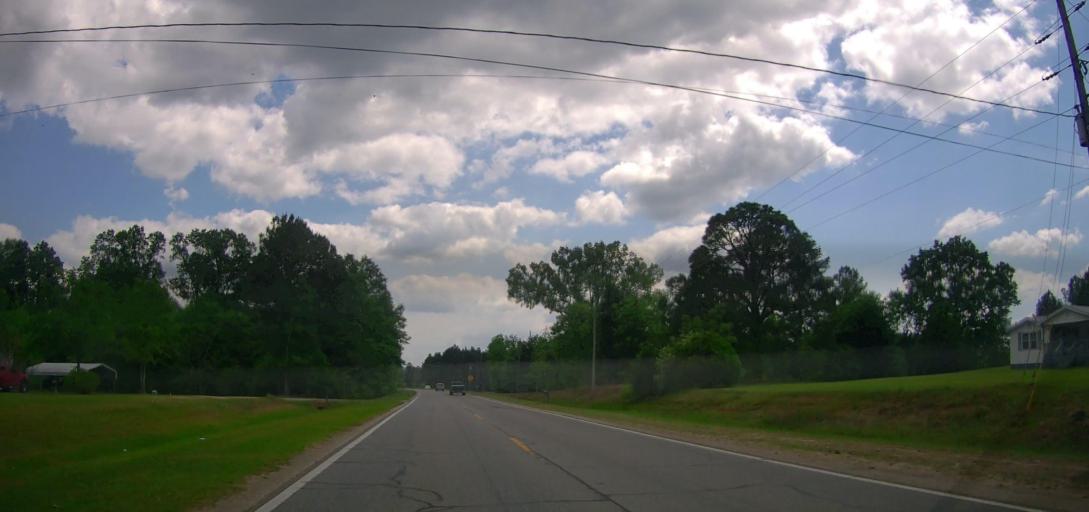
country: US
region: Georgia
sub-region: Laurens County
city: East Dublin
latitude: 32.5011
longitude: -82.8334
